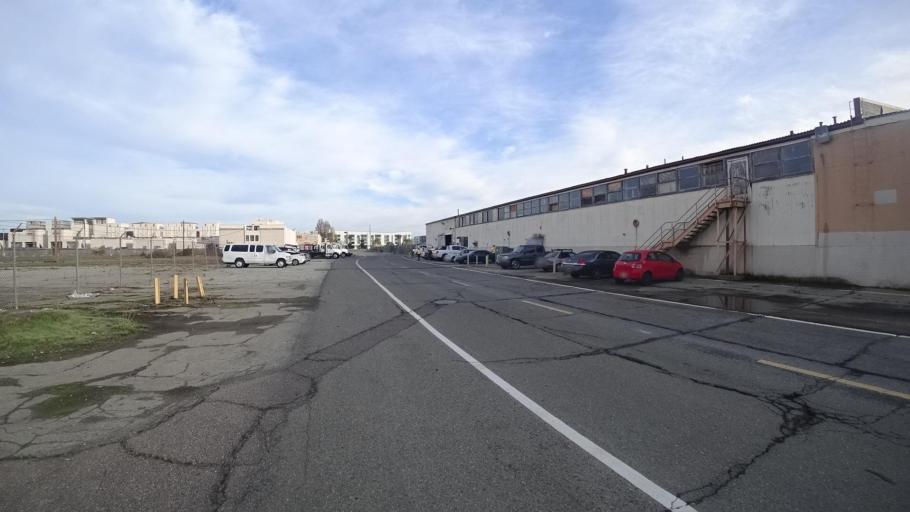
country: US
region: California
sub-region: Alameda County
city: Oakland
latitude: 37.7774
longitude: -122.2960
